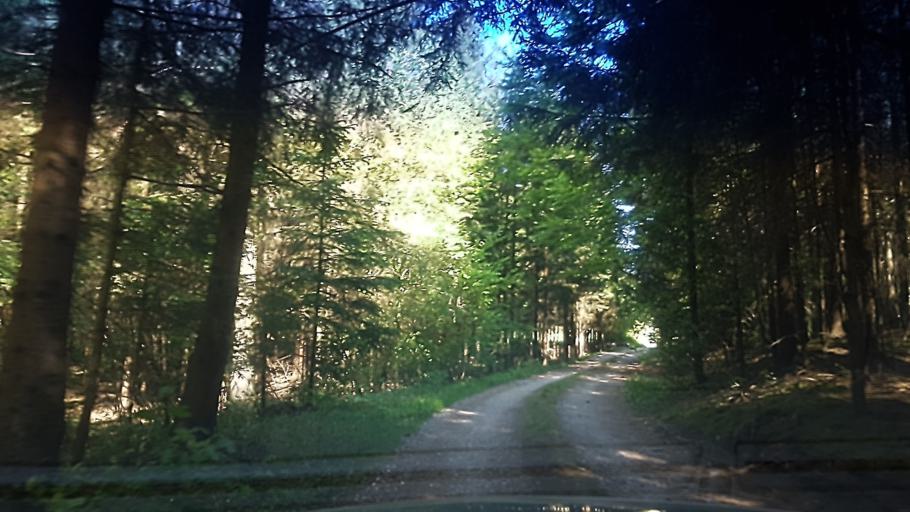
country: DE
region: Bavaria
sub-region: Upper Franconia
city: Wattendorf
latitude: 49.9954
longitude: 11.1078
